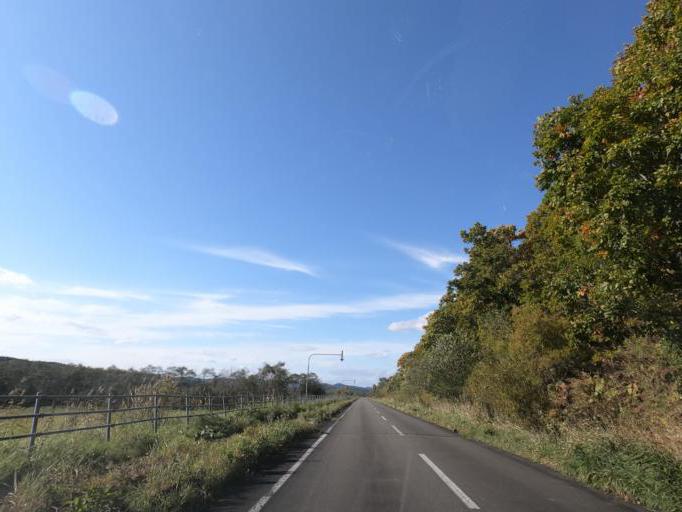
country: JP
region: Hokkaido
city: Obihiro
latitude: 42.6313
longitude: 143.5231
